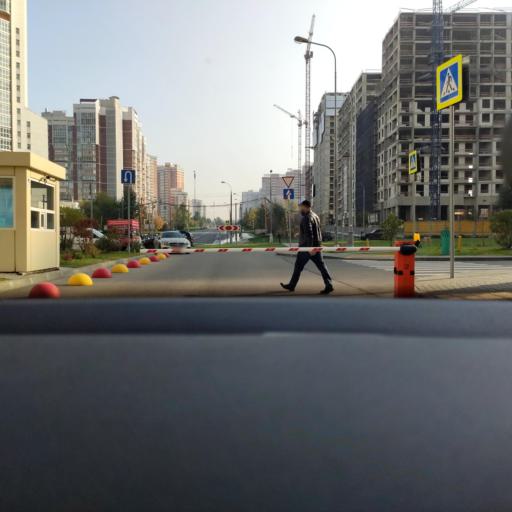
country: RU
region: Moscow
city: Ramenki
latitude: 55.7037
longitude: 37.4923
